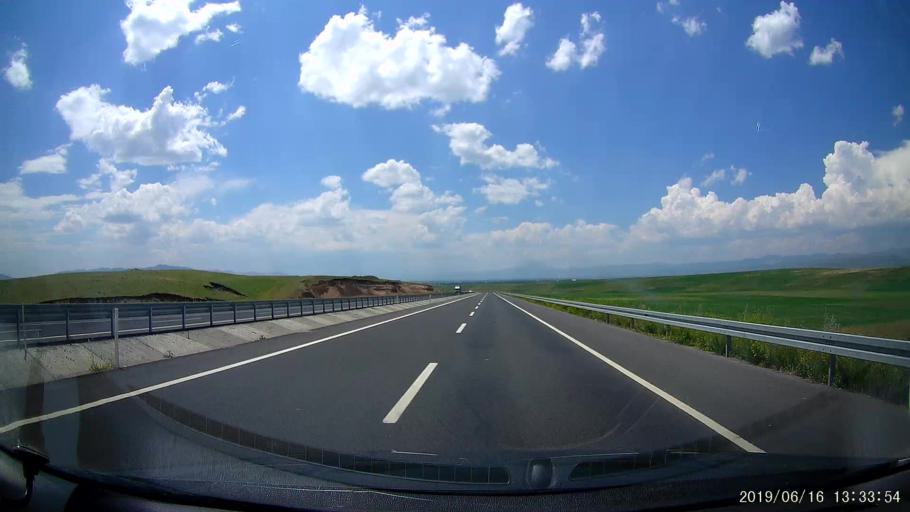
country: TR
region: Agri
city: Agri
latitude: 39.7095
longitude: 43.1418
